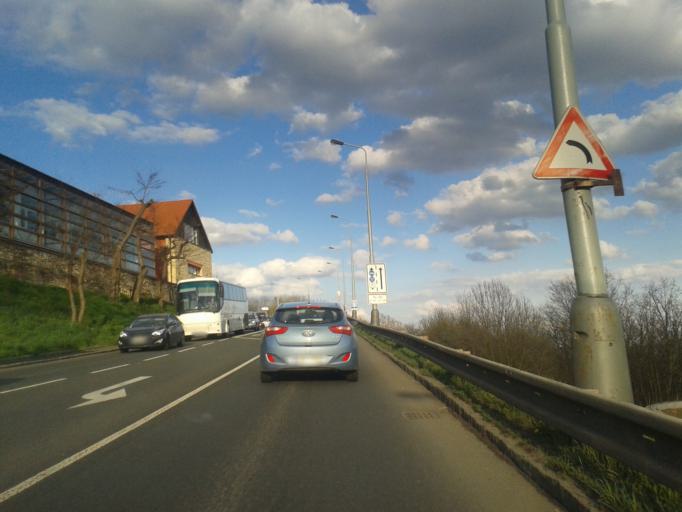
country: CZ
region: Central Bohemia
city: Horomerice
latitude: 50.0759
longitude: 14.3457
